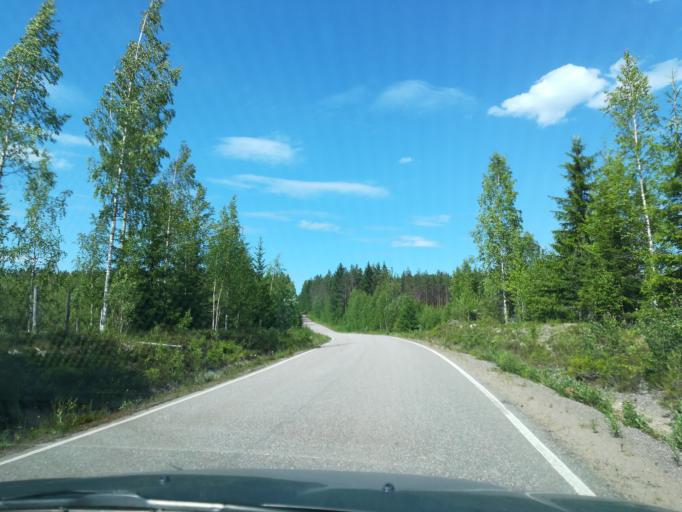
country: FI
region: South Karelia
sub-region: Imatra
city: Ruokolahti
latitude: 61.4781
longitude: 28.8735
